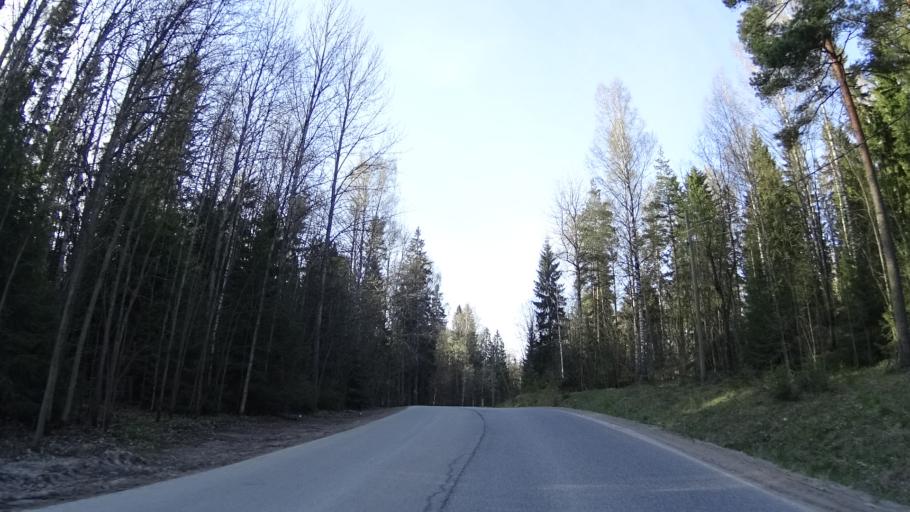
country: FI
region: Uusimaa
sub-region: Helsinki
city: Kilo
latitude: 60.3013
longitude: 24.7954
